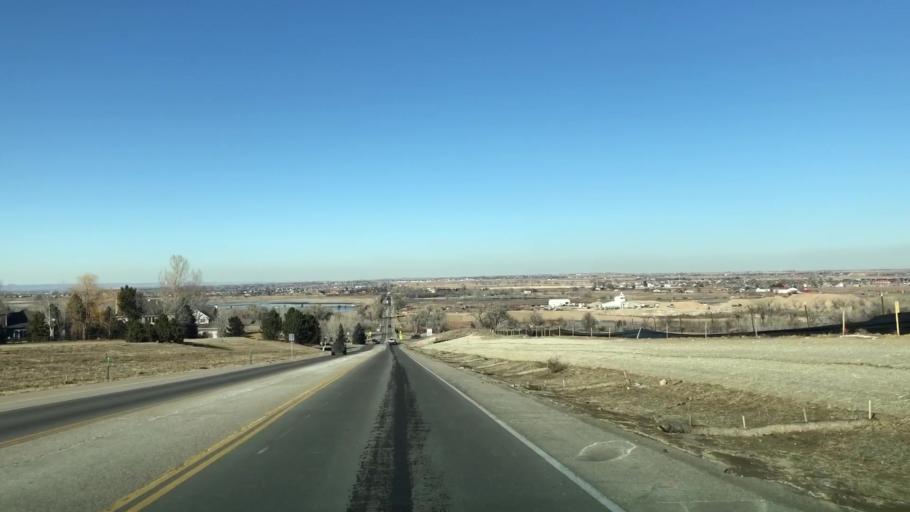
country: US
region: Colorado
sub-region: Weld County
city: Windsor
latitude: 40.4679
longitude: -104.9441
